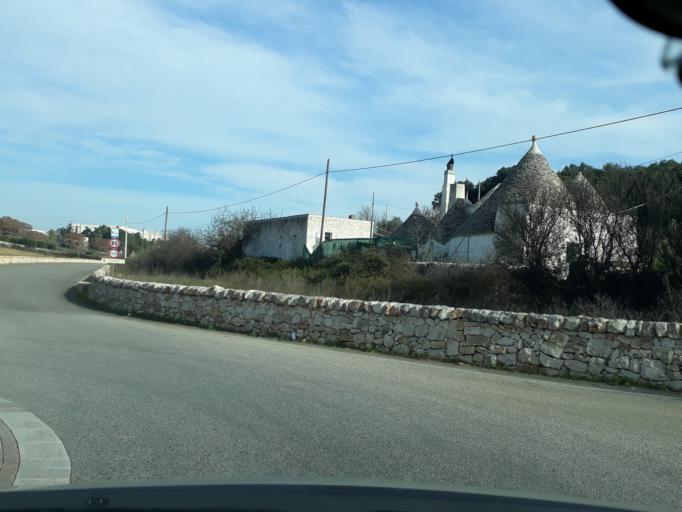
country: IT
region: Apulia
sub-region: Provincia di Bari
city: Locorotondo
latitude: 40.7493
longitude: 17.3348
